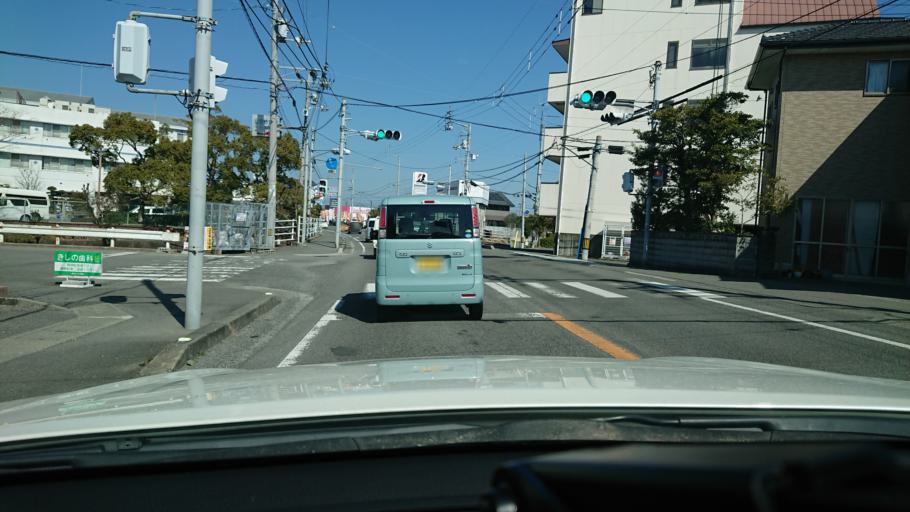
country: JP
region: Tokushima
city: Narutocho-mitsuishi
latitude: 34.1427
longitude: 134.5934
